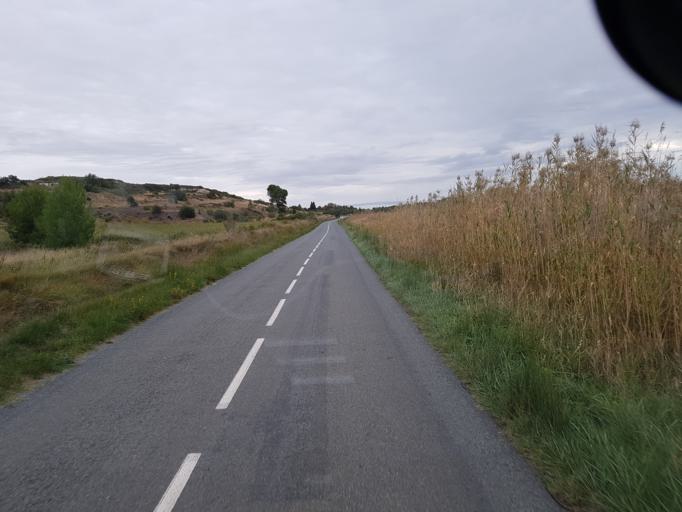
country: FR
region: Languedoc-Roussillon
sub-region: Departement de l'Aude
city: Narbonne
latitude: 43.1403
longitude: 2.9805
